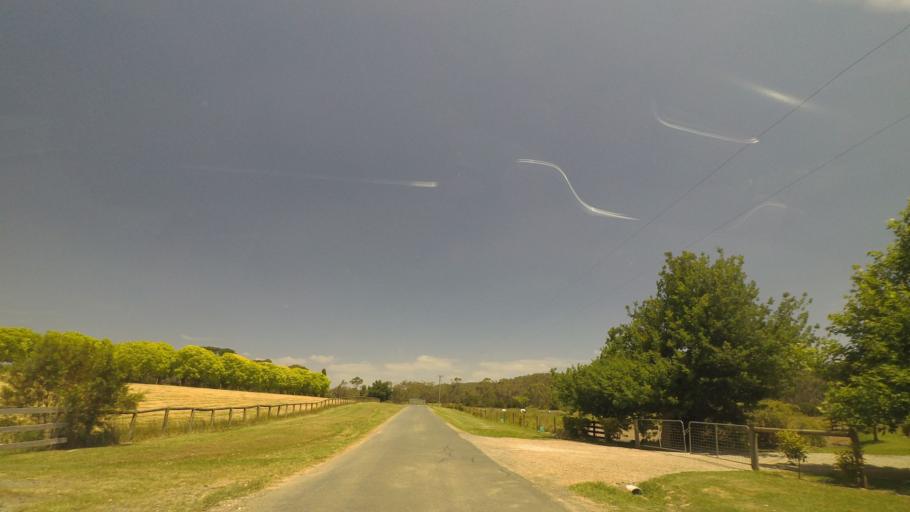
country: AU
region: Victoria
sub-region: Yarra Ranges
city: Chirnside Park
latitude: -37.7457
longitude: 145.2937
